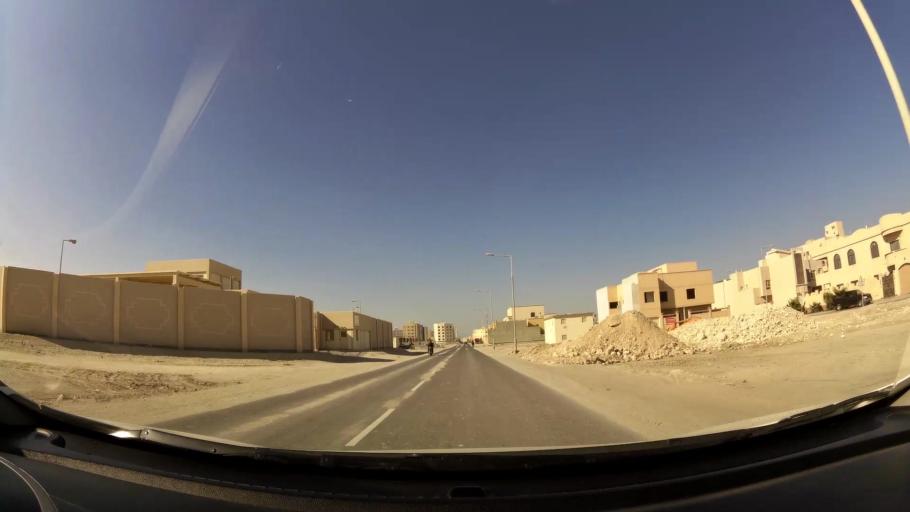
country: BH
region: Muharraq
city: Al Hadd
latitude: 26.2343
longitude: 50.6480
